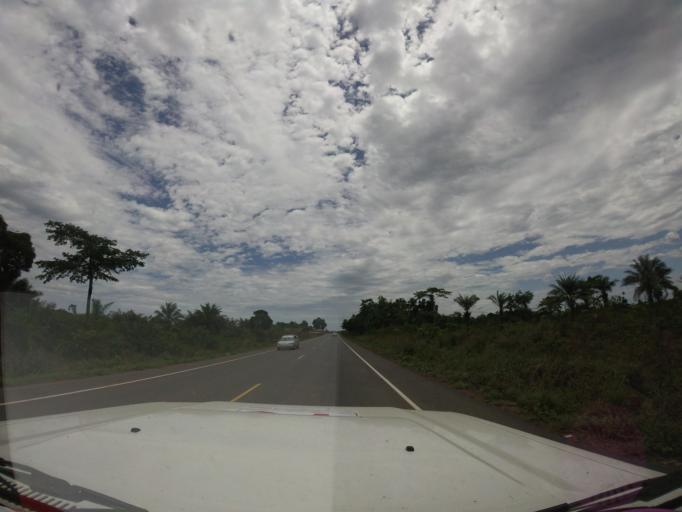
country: LR
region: Margibi
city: Kakata
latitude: 6.6070
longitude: -10.2756
